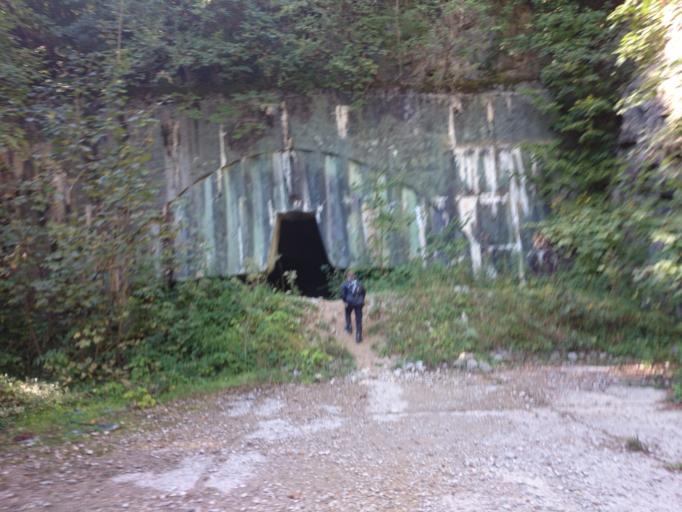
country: BA
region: Federation of Bosnia and Herzegovina
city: Izacic
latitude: 44.8358
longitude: 15.7560
